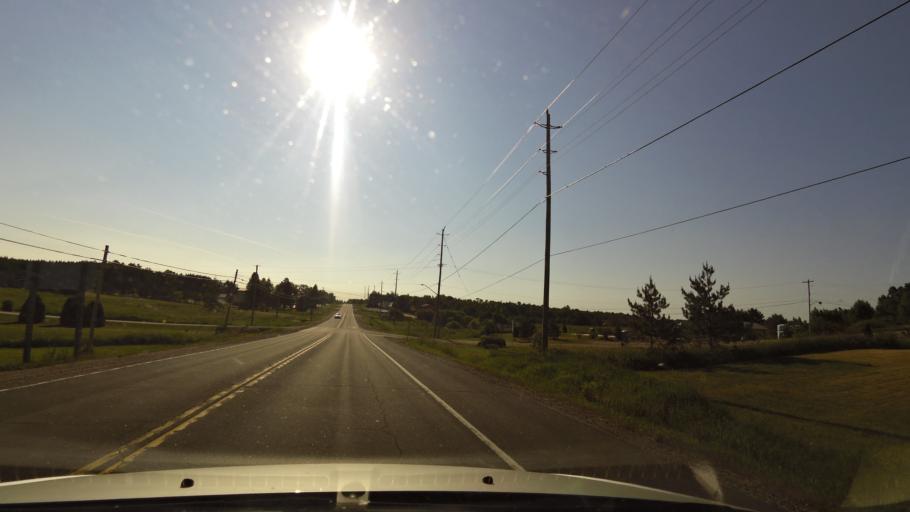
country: CA
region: Ontario
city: Greater Sudbury
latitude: 46.1047
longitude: -80.6148
